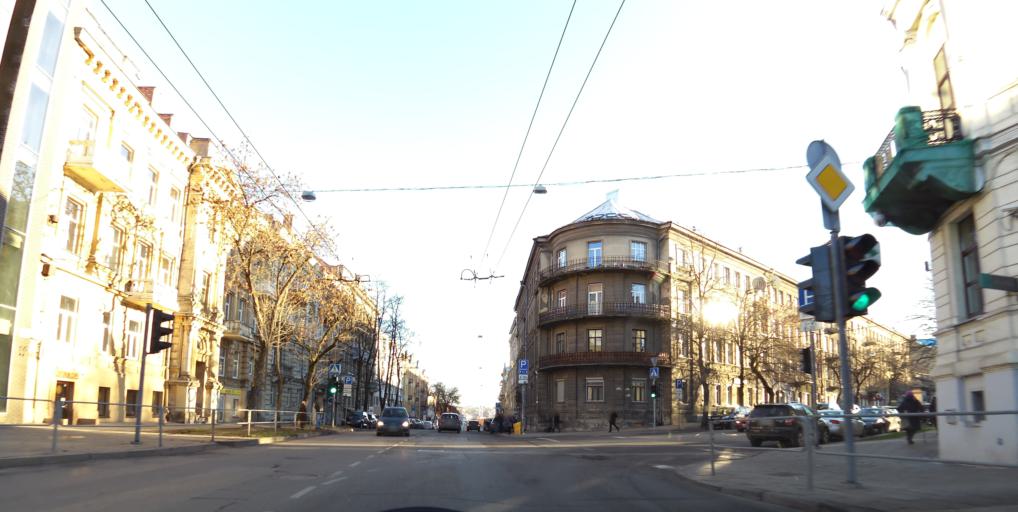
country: LT
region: Vilnius County
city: Naujamiestis
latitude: 54.6818
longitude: 25.2691
